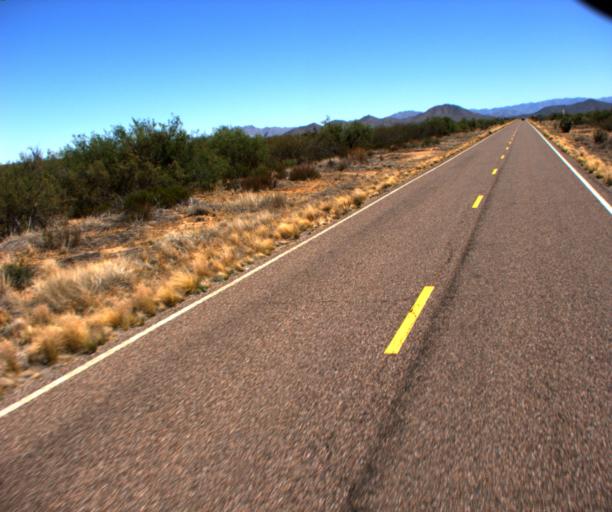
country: US
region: Arizona
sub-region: Yavapai County
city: Congress
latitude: 34.0507
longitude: -113.0580
